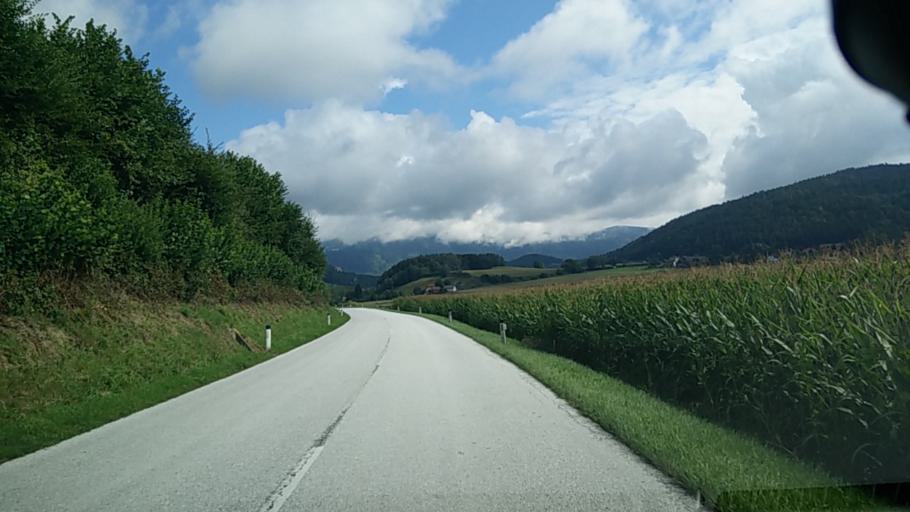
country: AT
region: Carinthia
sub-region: Politischer Bezirk Volkermarkt
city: Voelkermarkt
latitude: 46.6606
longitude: 14.5722
